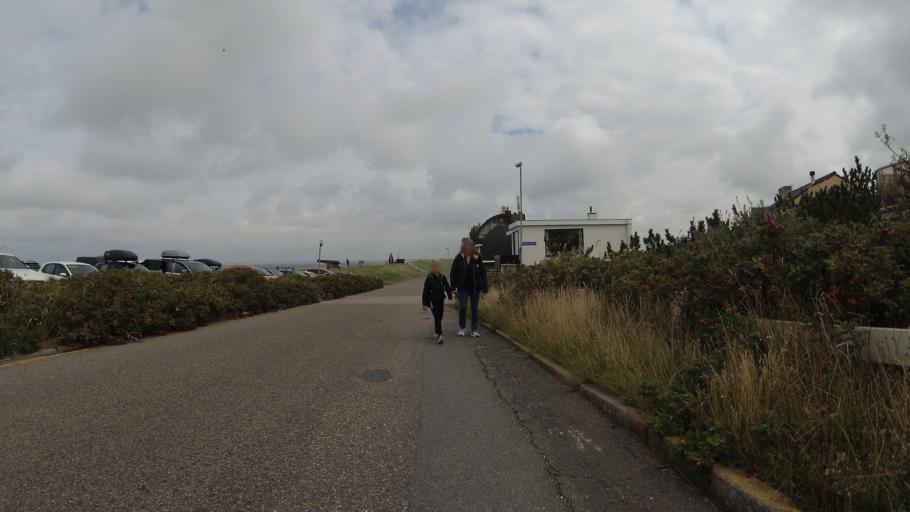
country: NL
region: North Holland
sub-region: Gemeente Den Helder
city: Den Helder
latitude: 52.9526
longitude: 4.7225
